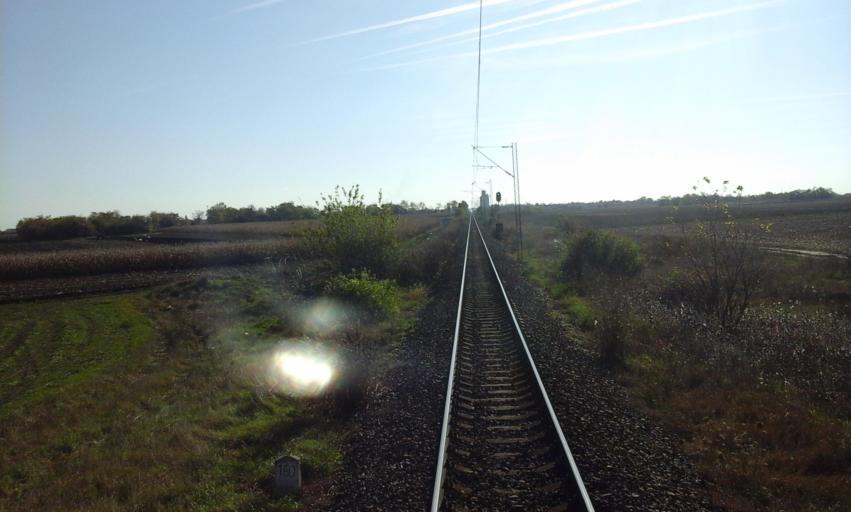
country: RS
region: Autonomna Pokrajina Vojvodina
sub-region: Severnobacki Okrug
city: Subotica
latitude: 45.9595
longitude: 19.6714
